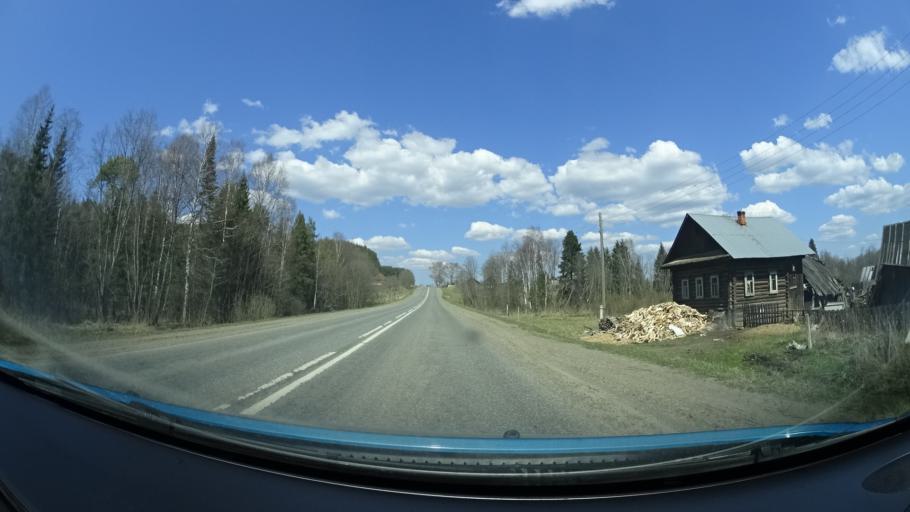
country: RU
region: Perm
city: Yugo-Kamskiy
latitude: 57.5468
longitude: 55.6842
